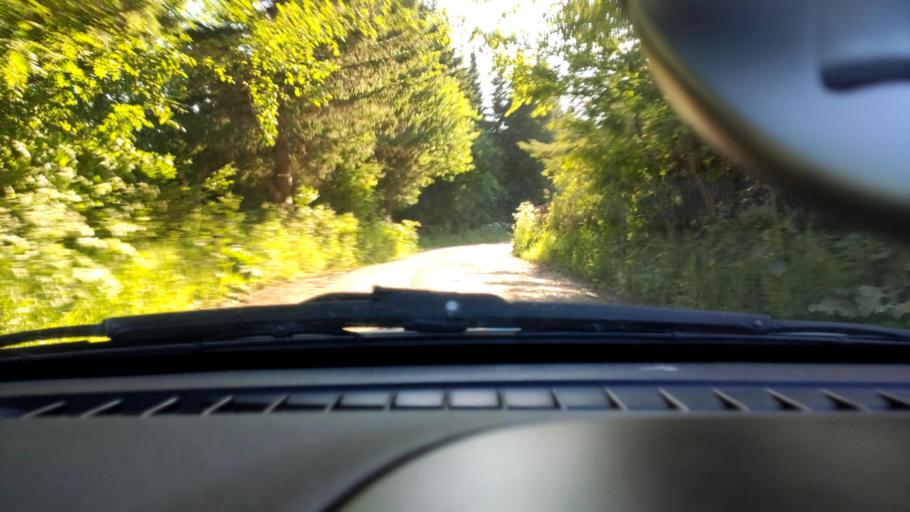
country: RU
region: Perm
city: Bershet'
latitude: 57.6983
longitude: 56.4132
